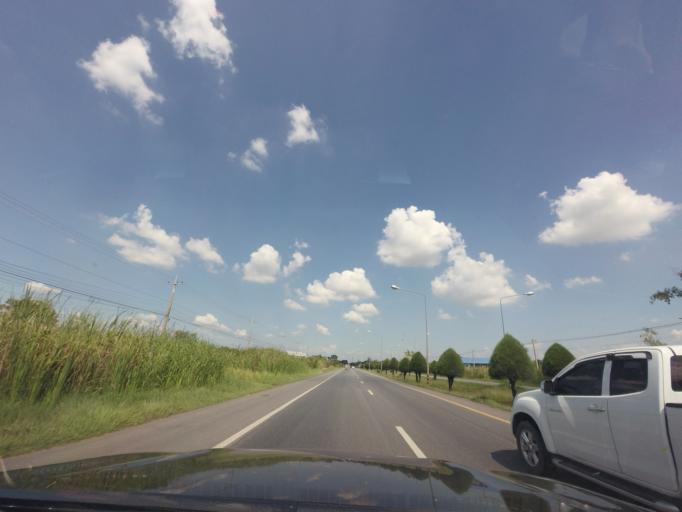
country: TH
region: Nakhon Ratchasima
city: Nakhon Ratchasima
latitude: 15.0551
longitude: 102.1472
